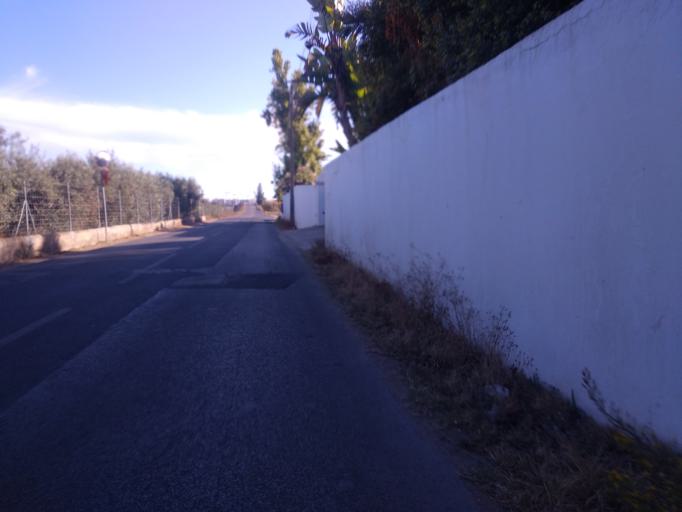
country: PT
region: Faro
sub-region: Faro
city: Faro
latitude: 37.0459
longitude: -7.9378
